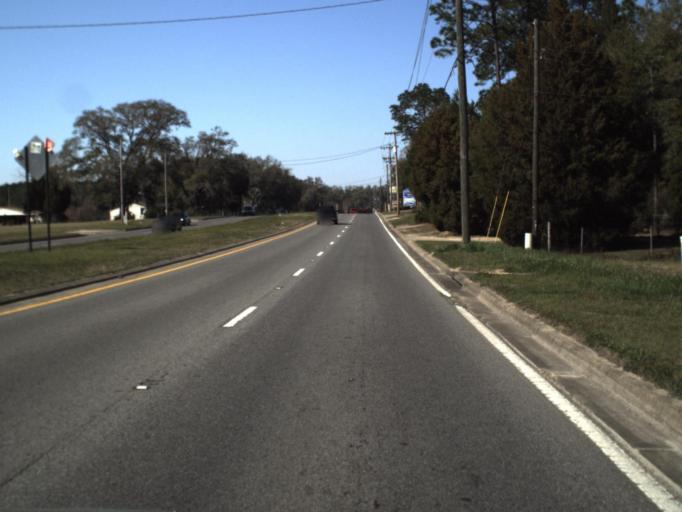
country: US
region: Florida
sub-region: Jackson County
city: Marianna
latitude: 30.7442
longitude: -85.1865
